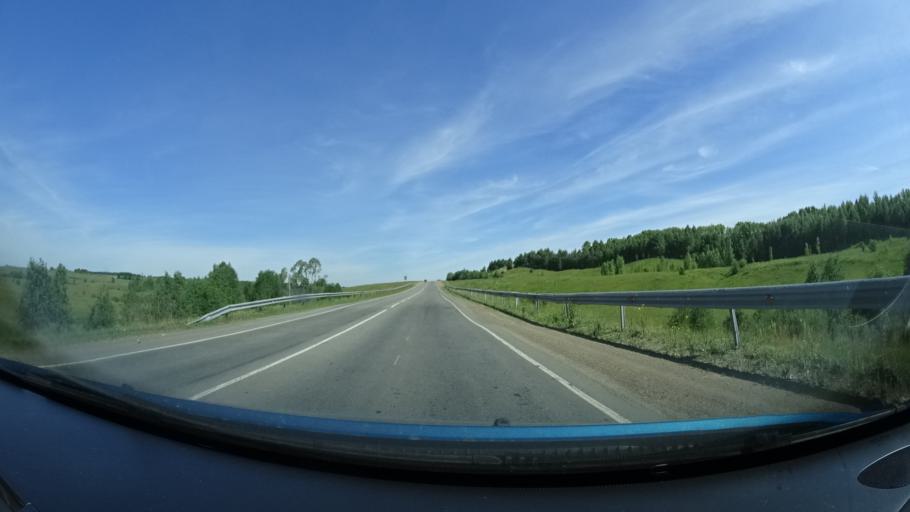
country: RU
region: Bashkortostan
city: Blagoveshchensk
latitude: 55.1131
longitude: 55.8414
